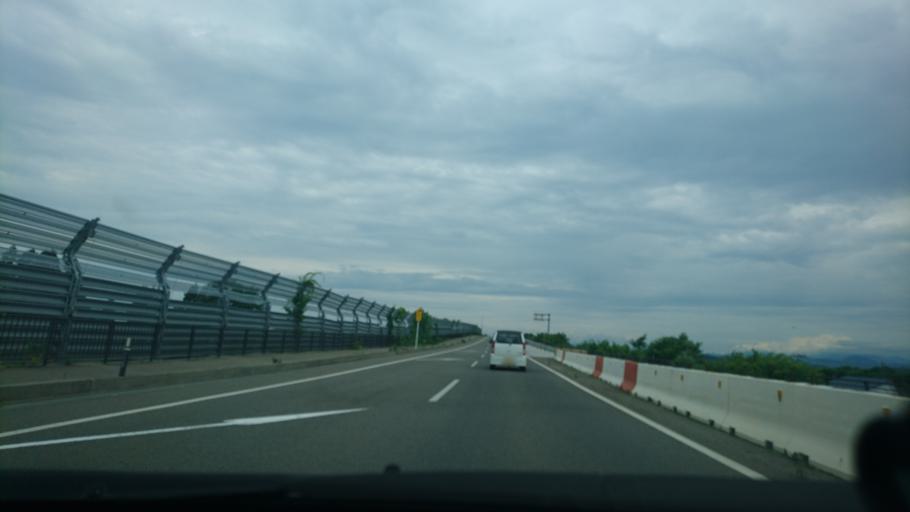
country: JP
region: Akita
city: Omagari
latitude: 39.4884
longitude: 140.4527
